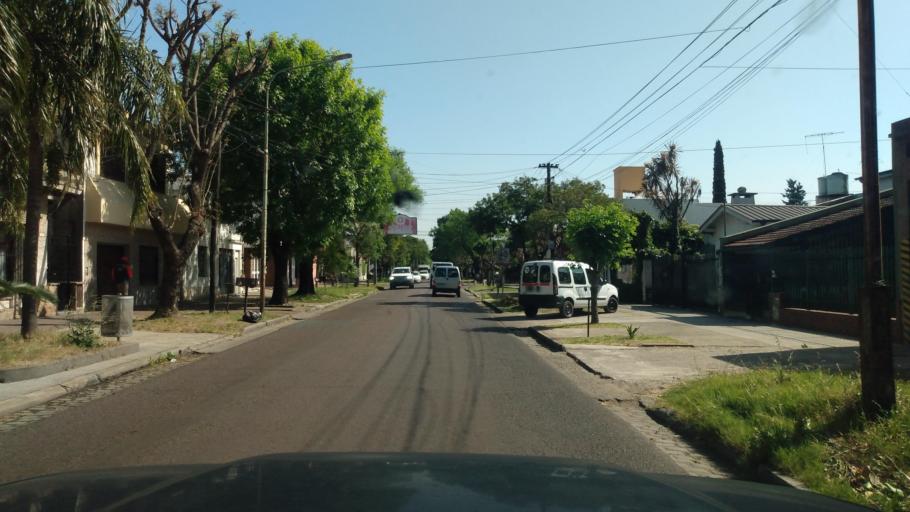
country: AR
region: Buenos Aires
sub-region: Partido de Moron
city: Moron
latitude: -34.6426
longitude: -58.5954
